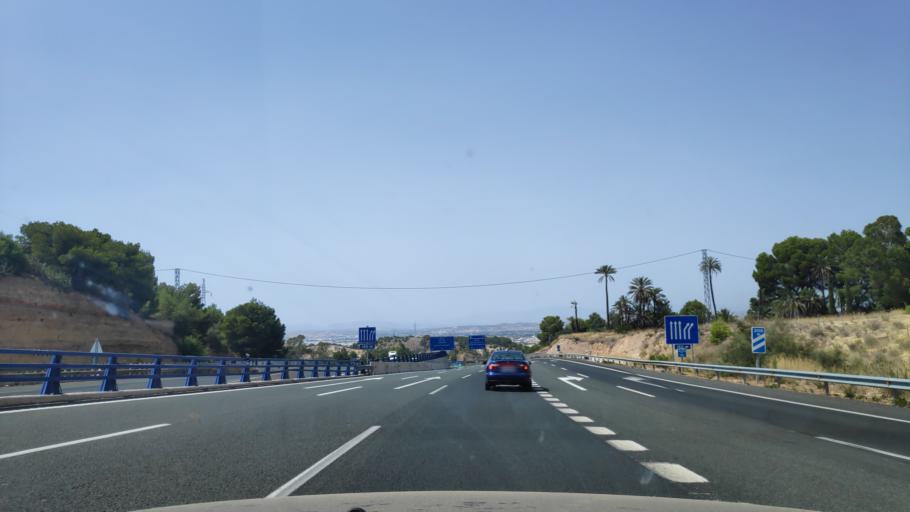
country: ES
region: Murcia
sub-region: Murcia
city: Alcantarilla
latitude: 37.9104
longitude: -1.1632
